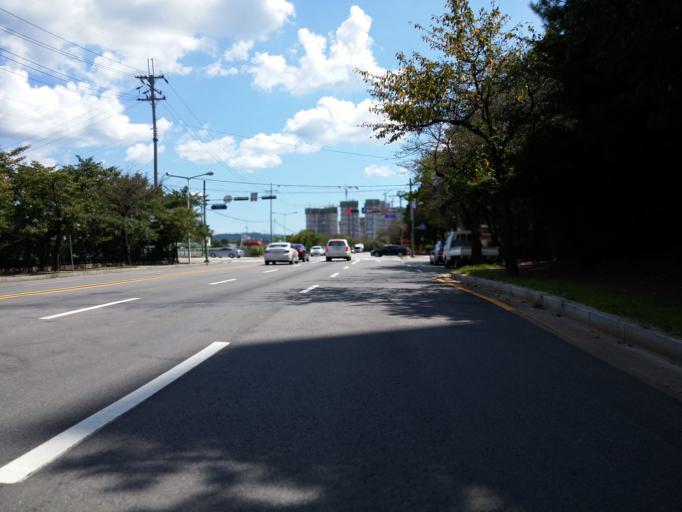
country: KR
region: Chungcheongbuk-do
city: Cheongju-si
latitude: 36.6125
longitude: 127.4957
